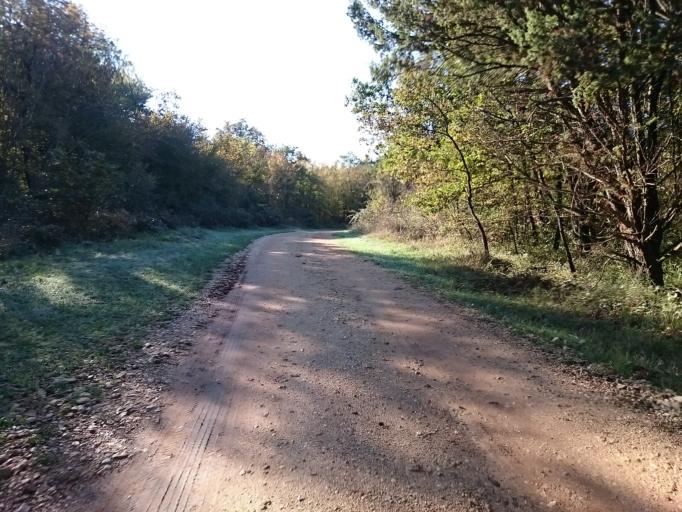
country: HR
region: Istarska
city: Novigrad
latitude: 45.2843
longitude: 13.6012
